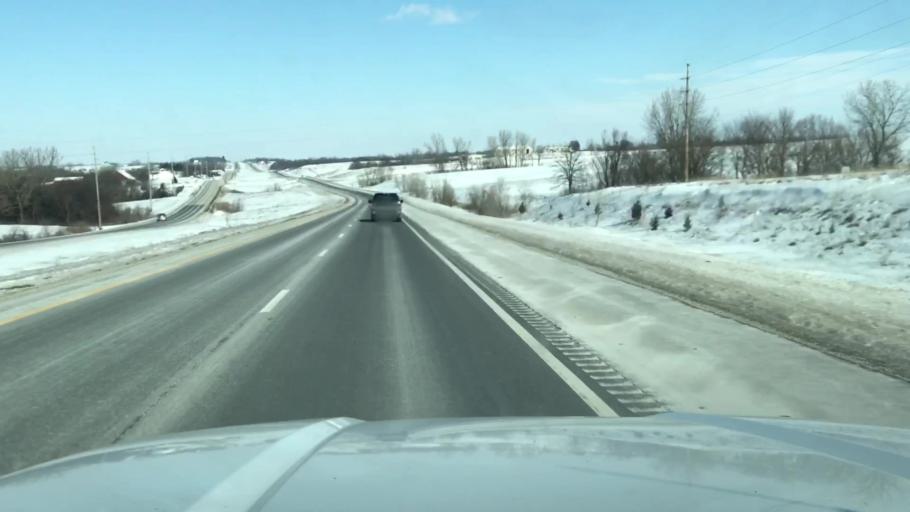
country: US
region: Missouri
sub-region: Nodaway County
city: Maryville
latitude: 40.1813
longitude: -94.8684
